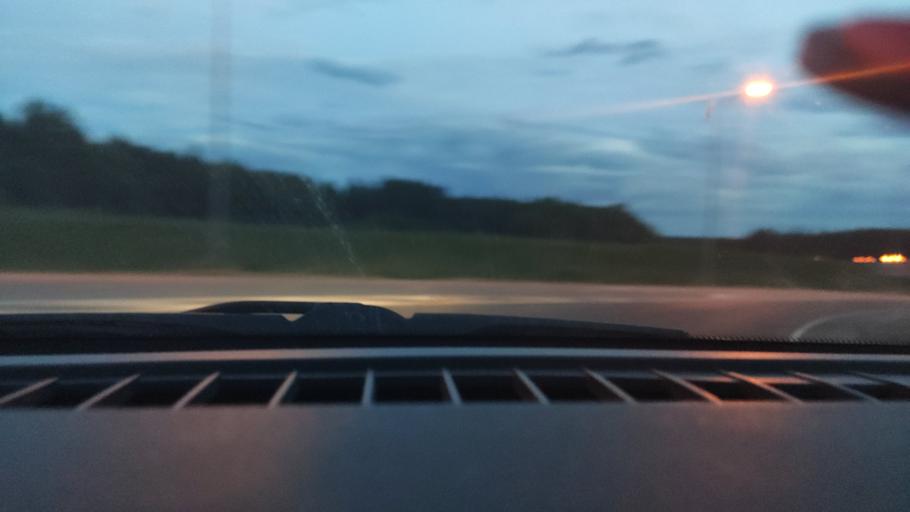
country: RU
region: Perm
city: Bershet'
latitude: 57.7353
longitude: 56.3486
